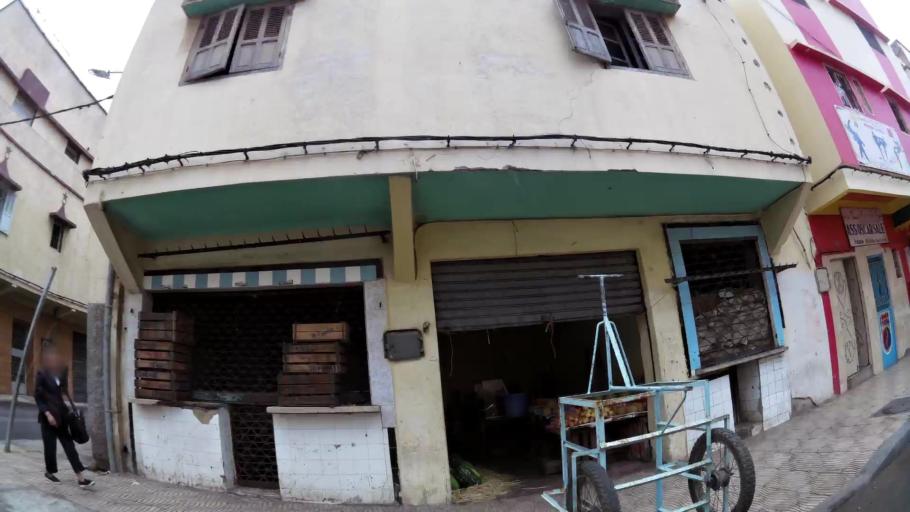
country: MA
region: Rabat-Sale-Zemmour-Zaer
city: Sale
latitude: 34.0388
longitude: -6.8127
